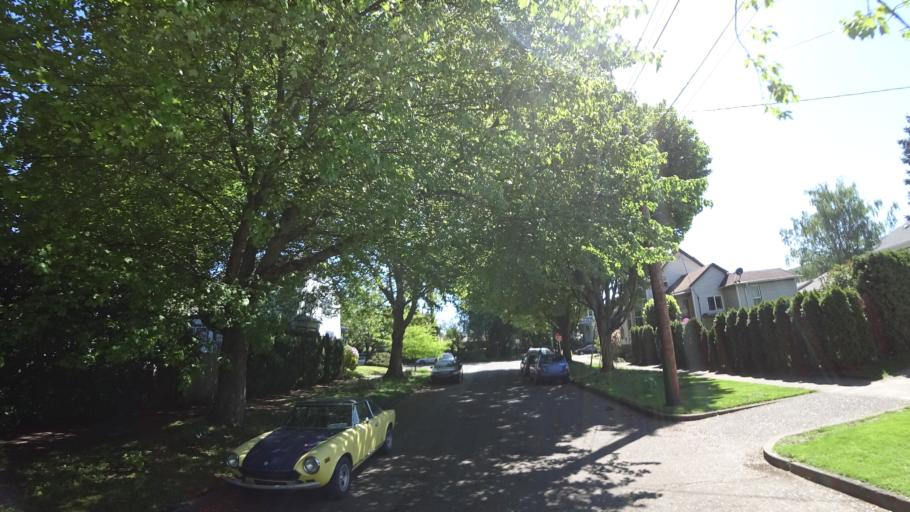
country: US
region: Oregon
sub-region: Multnomah County
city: Portland
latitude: 45.5156
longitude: -122.6244
